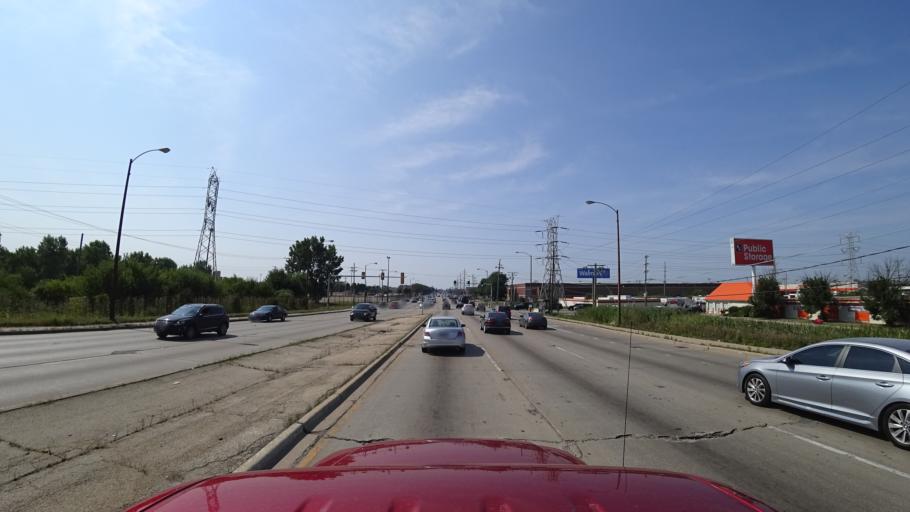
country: US
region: Illinois
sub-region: Cook County
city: Hometown
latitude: 41.7650
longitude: -87.7420
